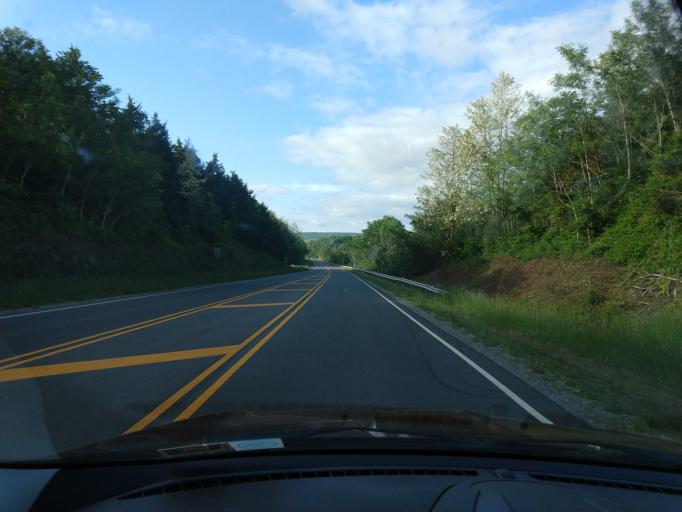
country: US
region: Virginia
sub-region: Wythe County
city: Wytheville
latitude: 36.8581
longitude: -80.9795
